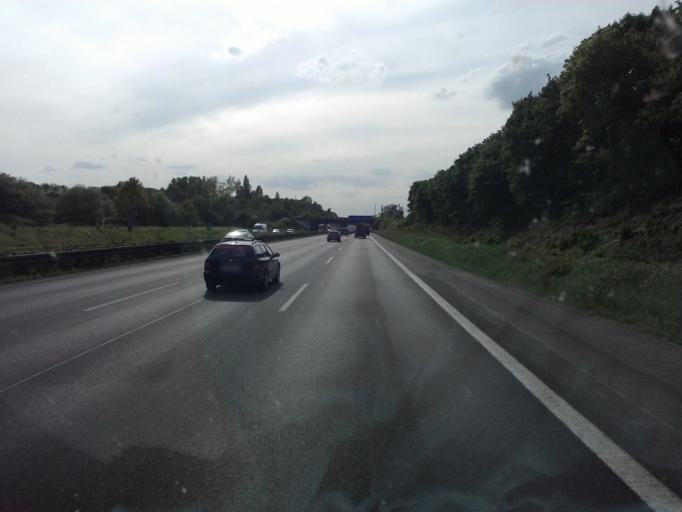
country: DE
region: North Rhine-Westphalia
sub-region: Regierungsbezirk Dusseldorf
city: Moers
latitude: 51.4370
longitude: 6.6603
